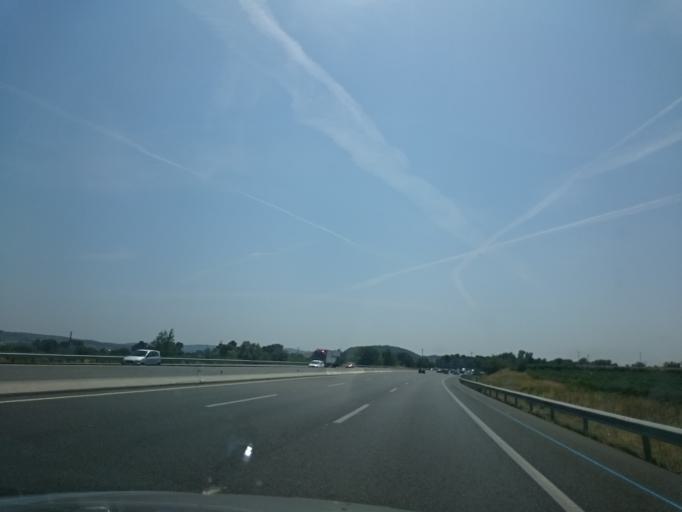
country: ES
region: Catalonia
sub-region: Provincia de Barcelona
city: Castellet
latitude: 41.3194
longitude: 1.6394
